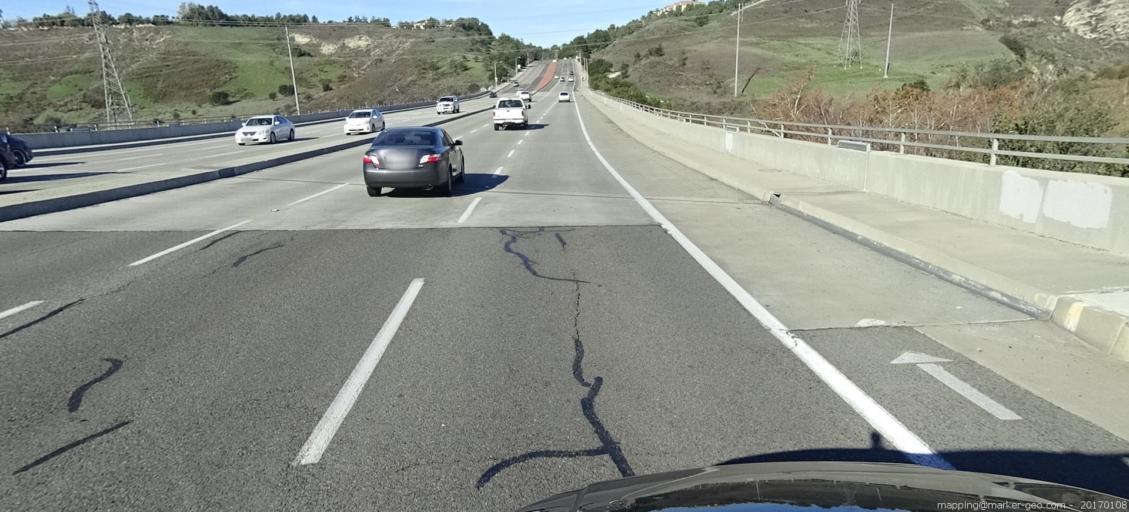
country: US
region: California
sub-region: Orange County
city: Las Flores
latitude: 33.5844
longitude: -117.6344
